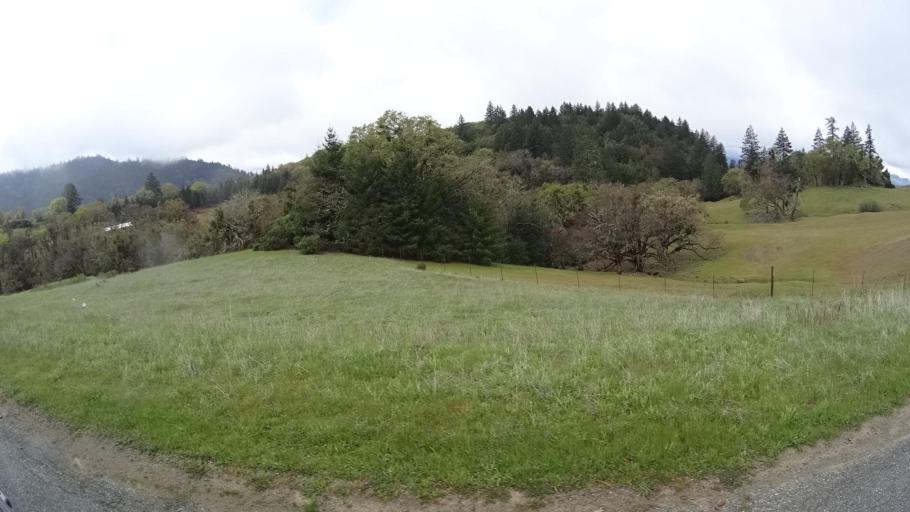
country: US
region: California
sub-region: Humboldt County
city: Redway
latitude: 40.1561
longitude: -123.5443
